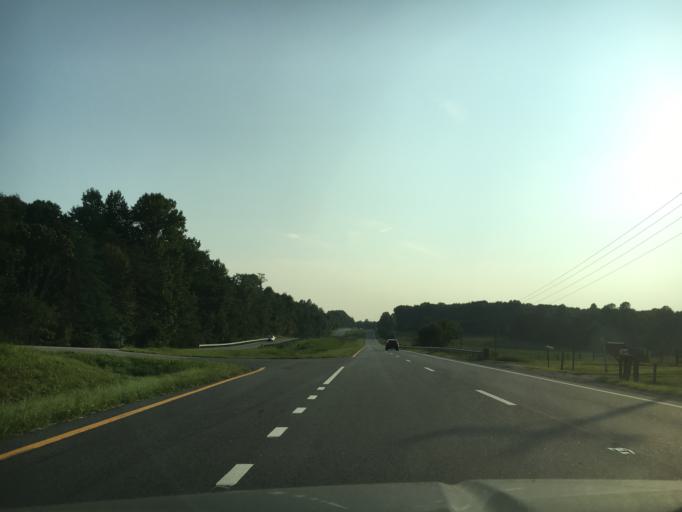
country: US
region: Virginia
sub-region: Prince Edward County
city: Hampden Sydney
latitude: 37.2713
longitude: -78.6416
